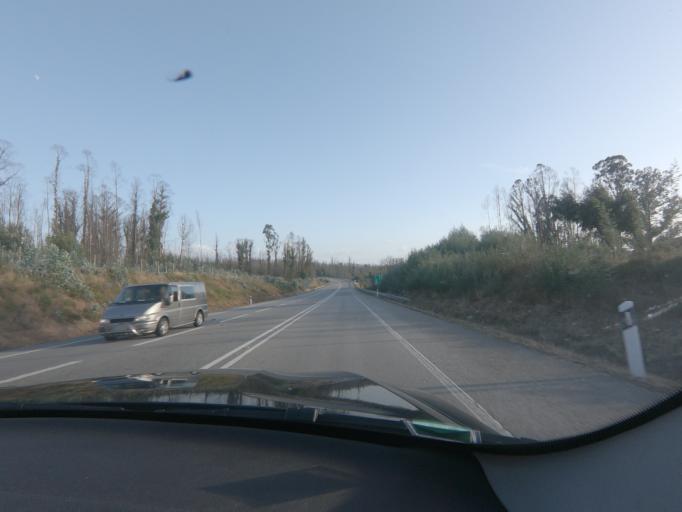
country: PT
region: Viseu
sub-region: Santa Comba Dao
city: Santa Comba Dao
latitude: 40.4528
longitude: -8.1050
